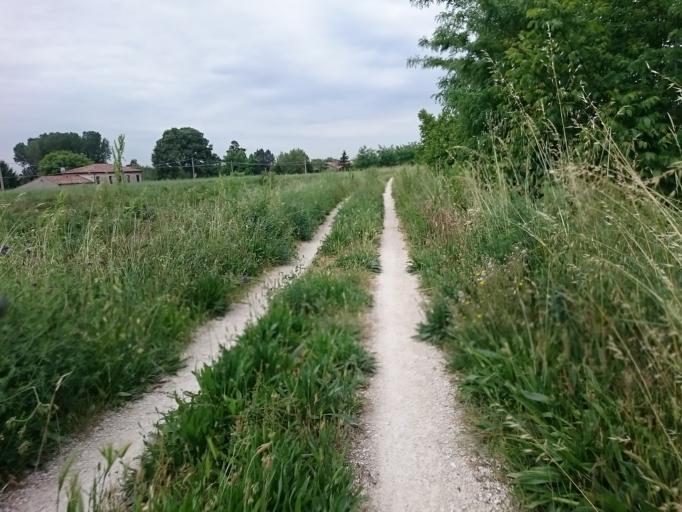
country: IT
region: Veneto
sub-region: Provincia di Padova
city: Baone
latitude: 45.2196
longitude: 11.7032
